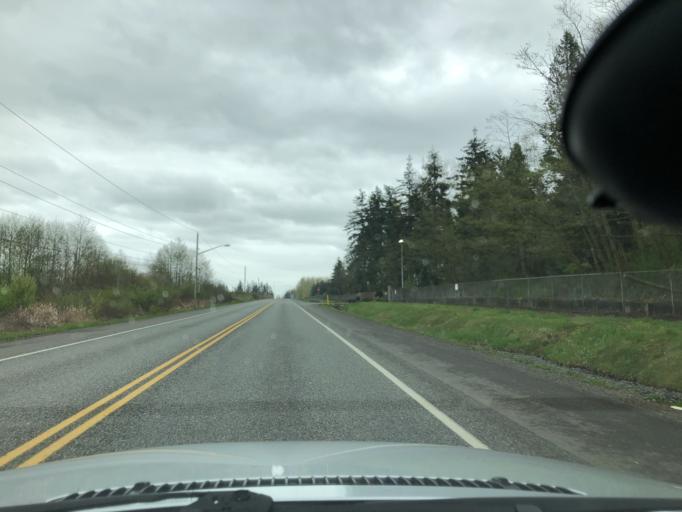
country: US
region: Washington
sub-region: Whatcom County
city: Birch Bay
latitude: 48.8922
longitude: -122.7352
